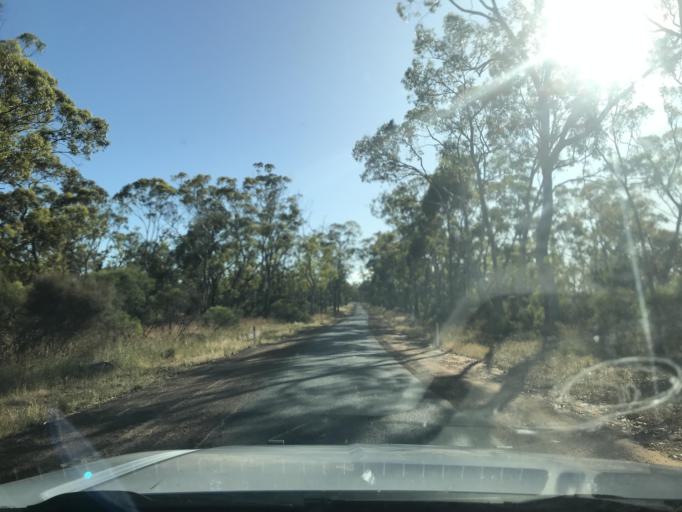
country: AU
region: Victoria
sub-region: Horsham
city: Horsham
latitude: -36.7036
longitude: 141.5078
